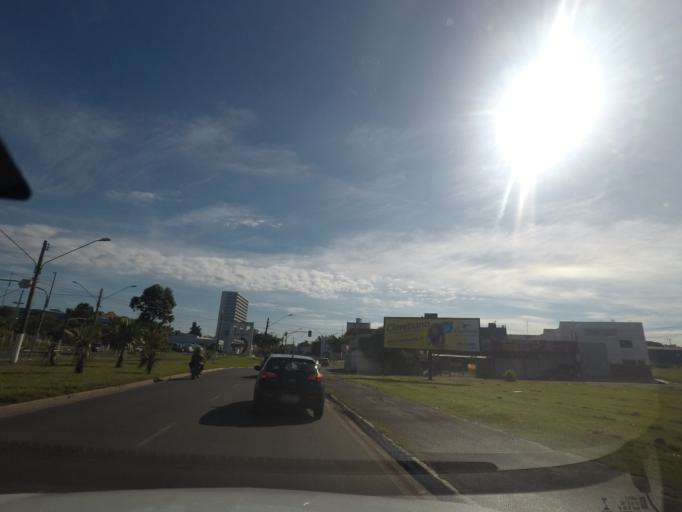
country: BR
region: Sao Paulo
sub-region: Rio Claro
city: Rio Claro
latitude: -22.4182
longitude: -47.5756
